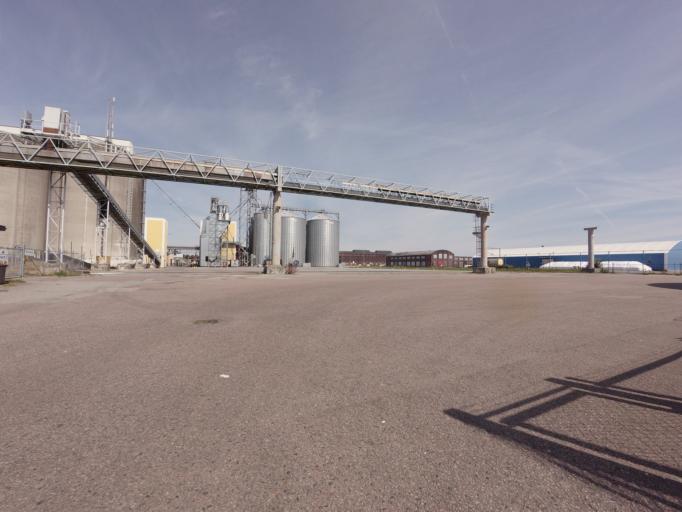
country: SE
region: Skane
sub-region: Landskrona
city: Landskrona
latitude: 55.8619
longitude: 12.8306
